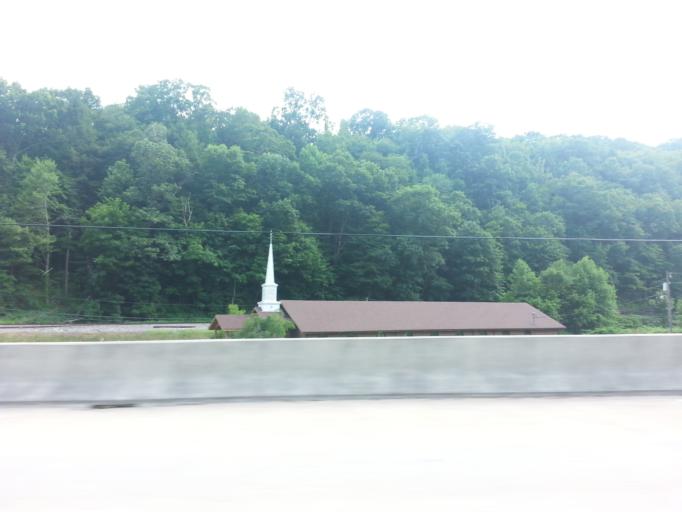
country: US
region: Kentucky
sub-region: Harlan County
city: Harlan
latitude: 36.8078
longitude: -83.3076
